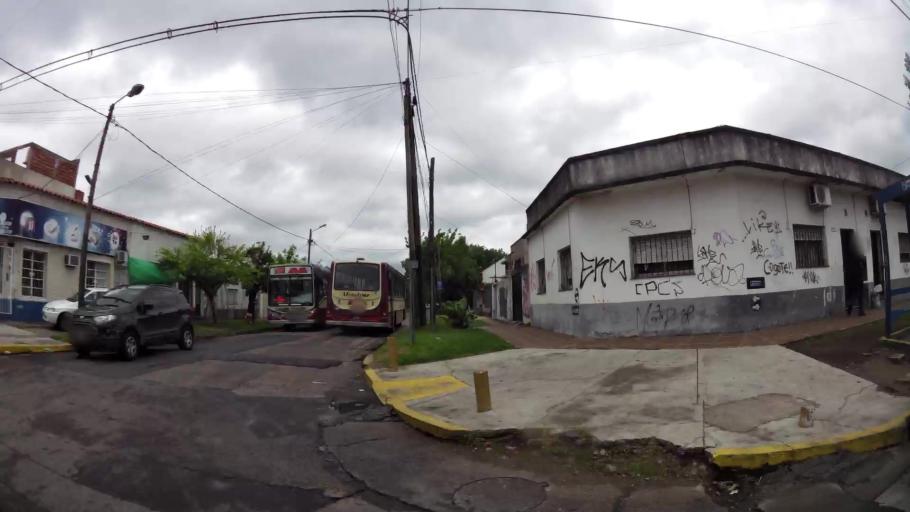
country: AR
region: Buenos Aires
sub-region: Partido de Lomas de Zamora
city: Lomas de Zamora
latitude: -34.7606
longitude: -58.3852
